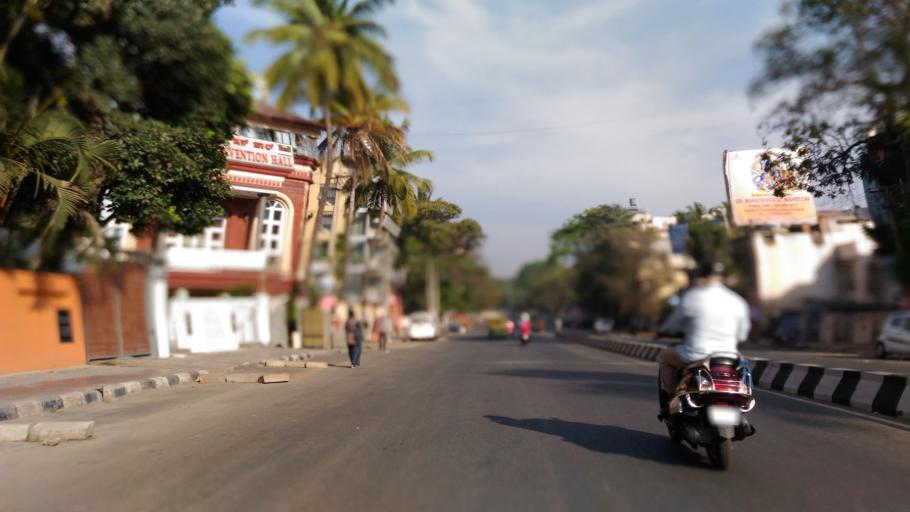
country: IN
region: Karnataka
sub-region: Bangalore Urban
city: Bangalore
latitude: 12.9377
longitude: 77.5792
